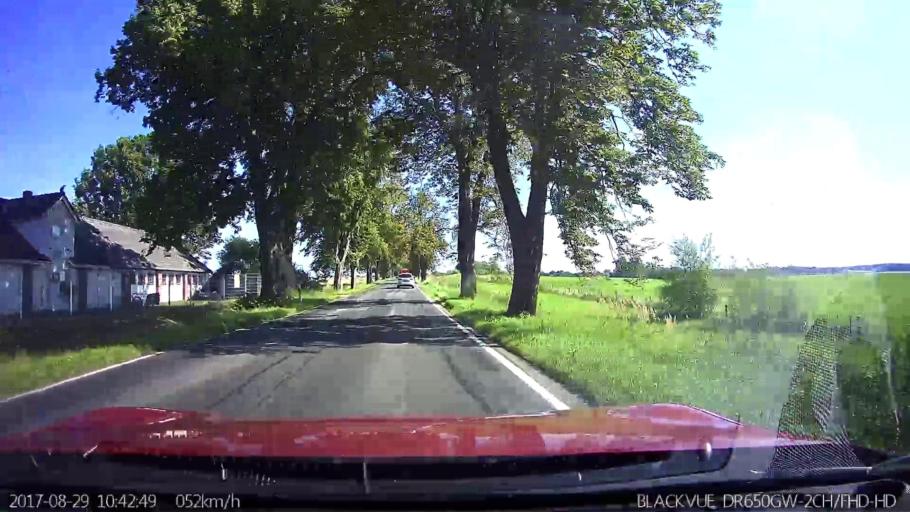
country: DE
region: Mecklenburg-Vorpommern
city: Franzburg
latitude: 54.1956
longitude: 12.8661
